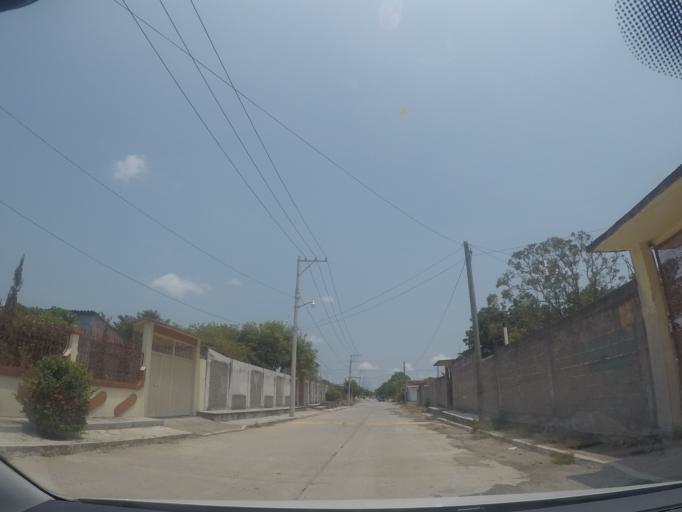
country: MX
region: Oaxaca
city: Asuncion Ixtaltepec
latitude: 16.5073
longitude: -95.0617
